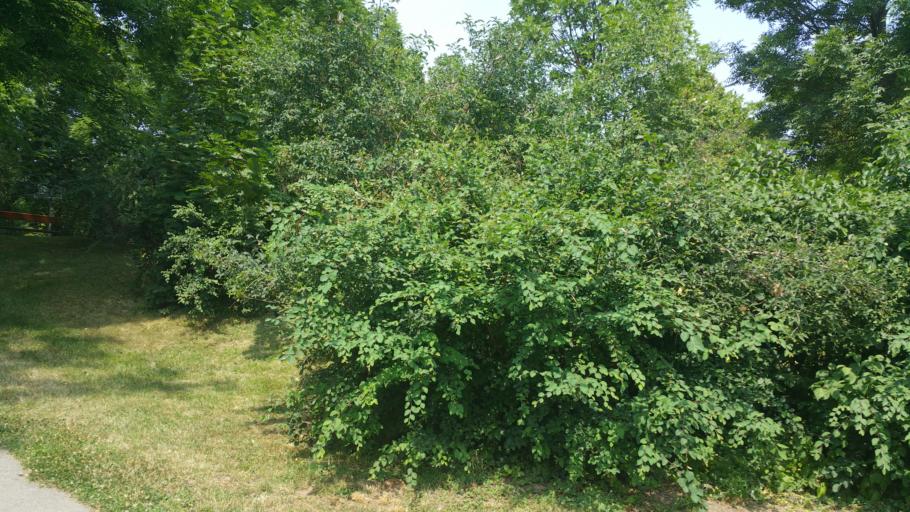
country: AT
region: Vienna
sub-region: Wien Stadt
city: Vienna
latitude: 48.2077
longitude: 16.2858
